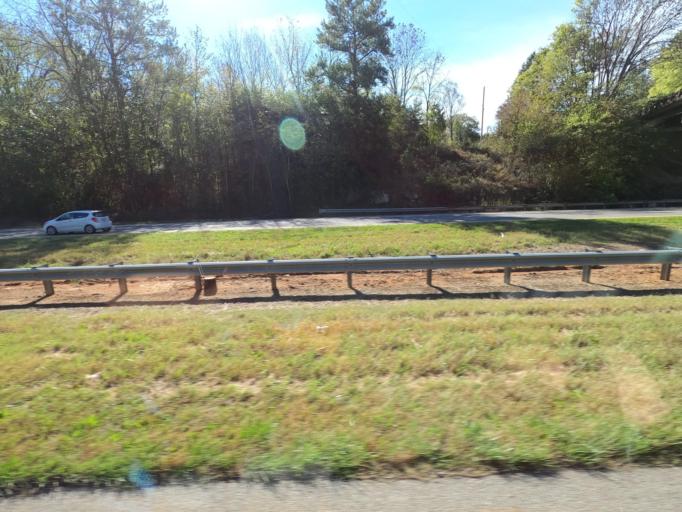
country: US
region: Tennessee
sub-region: Dickson County
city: Burns
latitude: 36.0181
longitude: -87.2415
